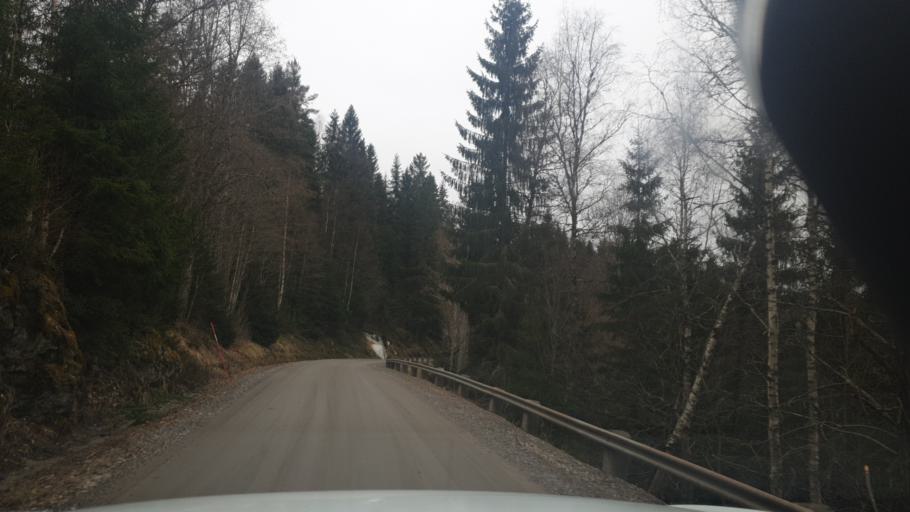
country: NO
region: Ostfold
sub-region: Romskog
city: Romskog
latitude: 59.7075
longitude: 11.9632
